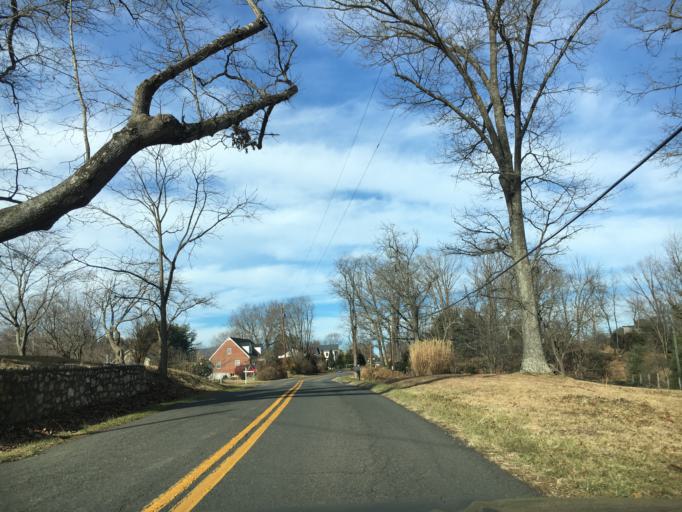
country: US
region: Virginia
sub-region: Warren County
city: Apple Mountain Lake
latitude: 38.8289
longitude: -77.9985
